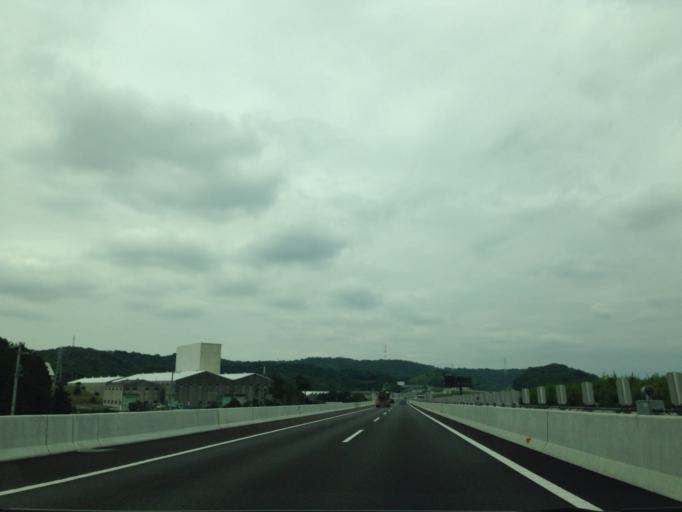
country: JP
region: Aichi
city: Gamagori
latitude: 34.9121
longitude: 137.2892
